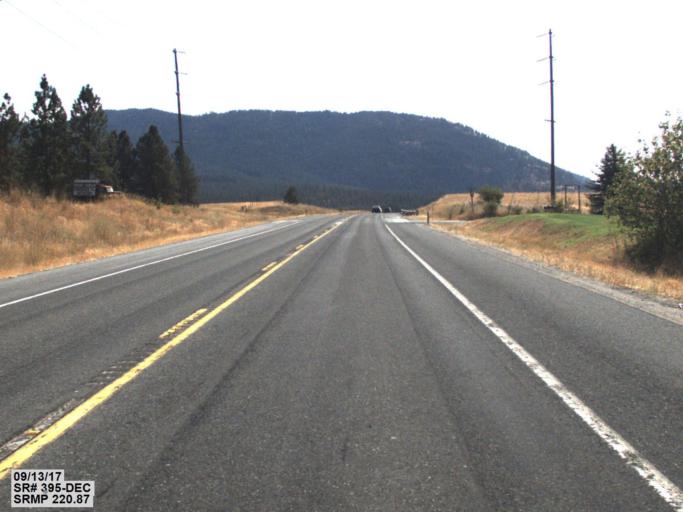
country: US
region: Washington
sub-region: Stevens County
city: Colville
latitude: 48.4283
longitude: -117.8572
